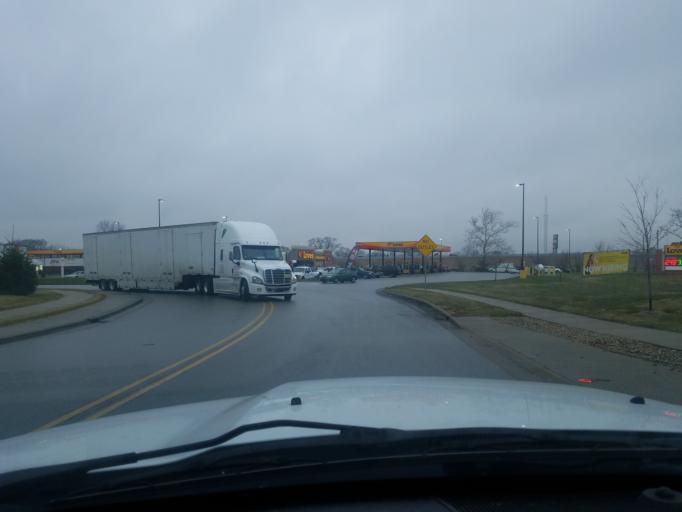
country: US
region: Indiana
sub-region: Madison County
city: Ingalls
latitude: 39.9915
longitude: -85.8436
